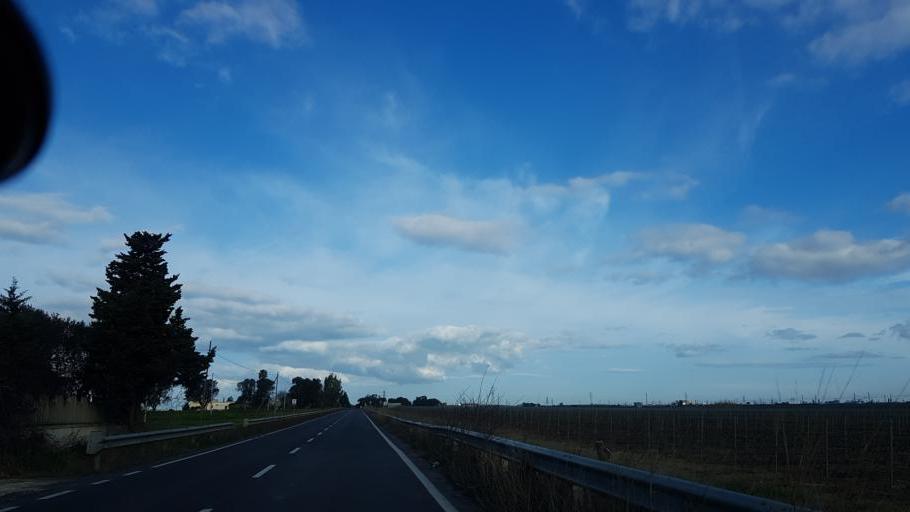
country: IT
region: Apulia
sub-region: Provincia di Brindisi
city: La Rosa
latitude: 40.5767
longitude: 17.9661
